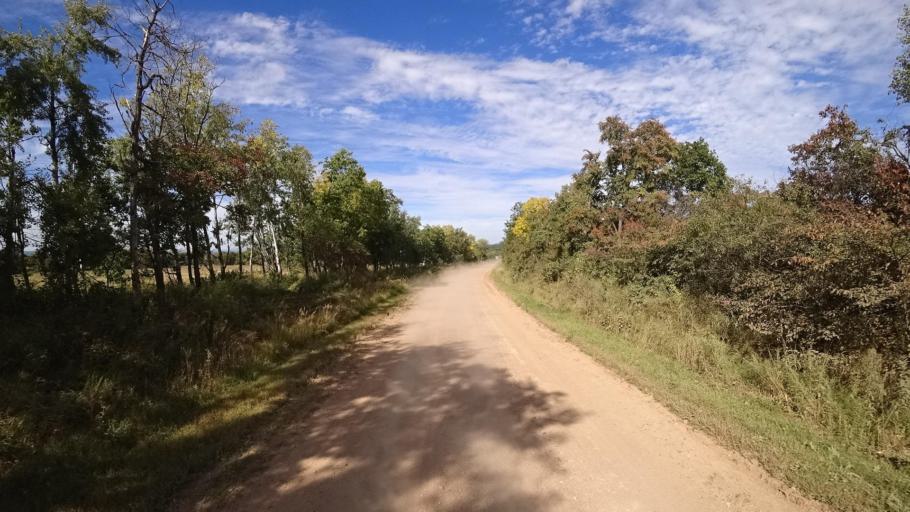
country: RU
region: Primorskiy
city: Yakovlevka
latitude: 44.4210
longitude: 133.5715
